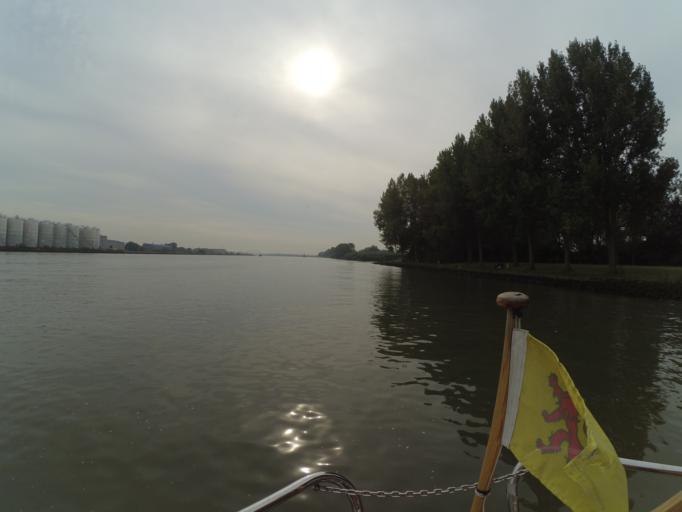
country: NL
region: South Holland
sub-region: Gemeente Ridderkerk
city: Ridderkerk
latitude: 51.8772
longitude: 4.6276
